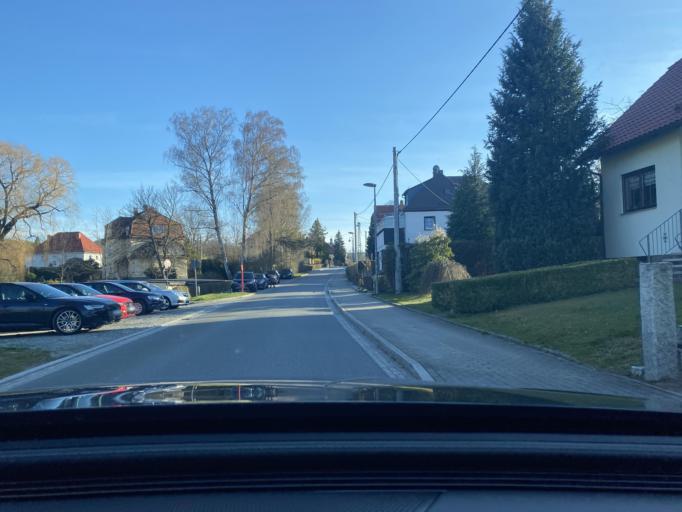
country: DE
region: Saxony
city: Sohland
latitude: 51.0510
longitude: 14.4311
